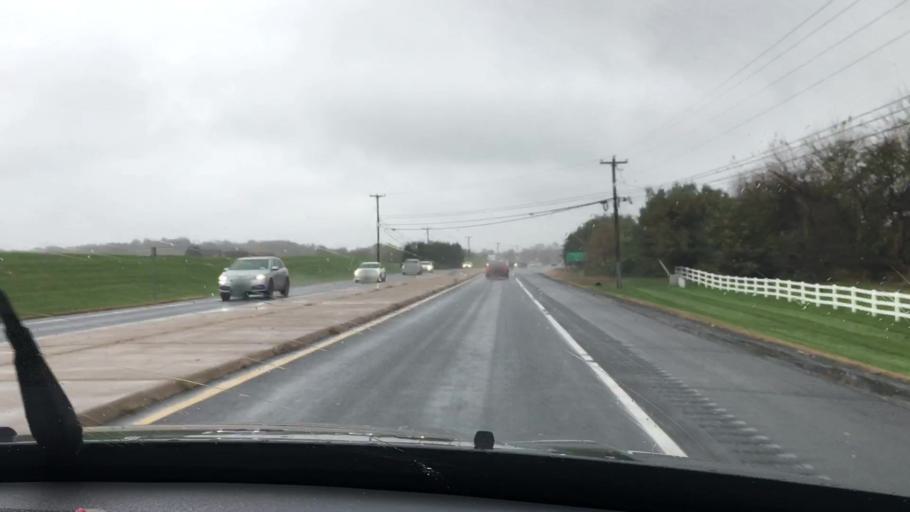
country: US
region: Virginia
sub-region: Loudoun County
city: Leesburg
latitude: 39.1498
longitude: -77.5414
